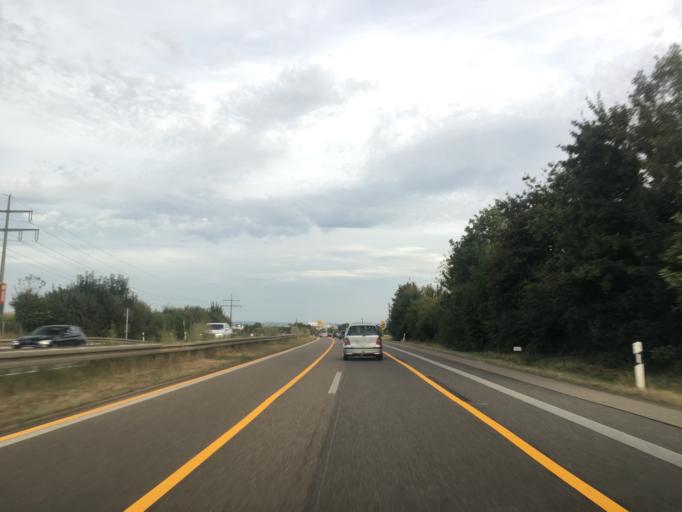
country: DE
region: Baden-Wuerttemberg
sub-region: Regierungsbezirk Stuttgart
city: Filderstadt
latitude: 48.6684
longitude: 9.1943
